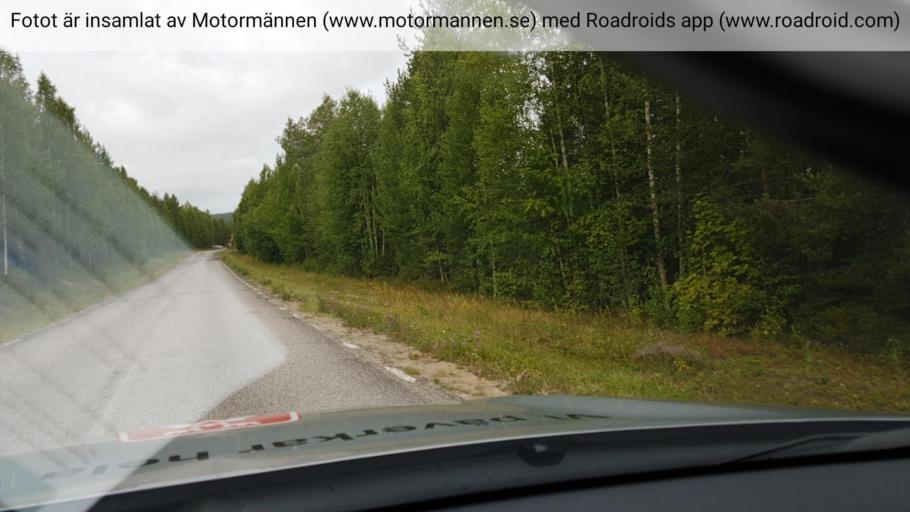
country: SE
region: Norrbotten
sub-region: Bodens Kommun
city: Saevast
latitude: 65.6687
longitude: 21.6902
